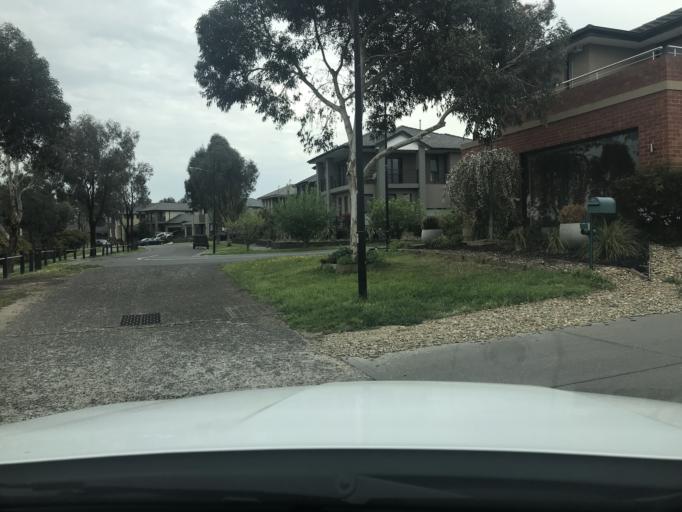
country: AU
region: Victoria
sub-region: Hume
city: Roxburgh Park
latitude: -37.5967
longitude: 144.9088
